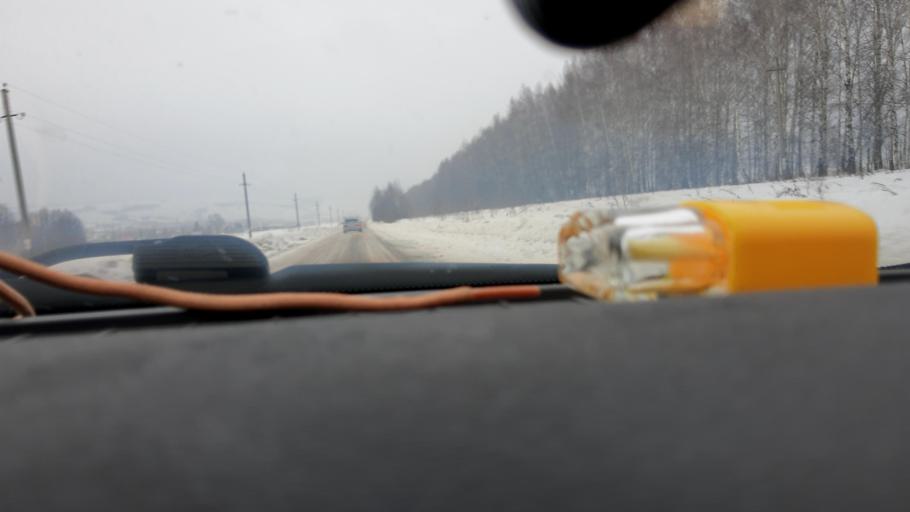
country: RU
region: Bashkortostan
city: Ulukulevo
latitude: 54.5649
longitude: 56.4322
